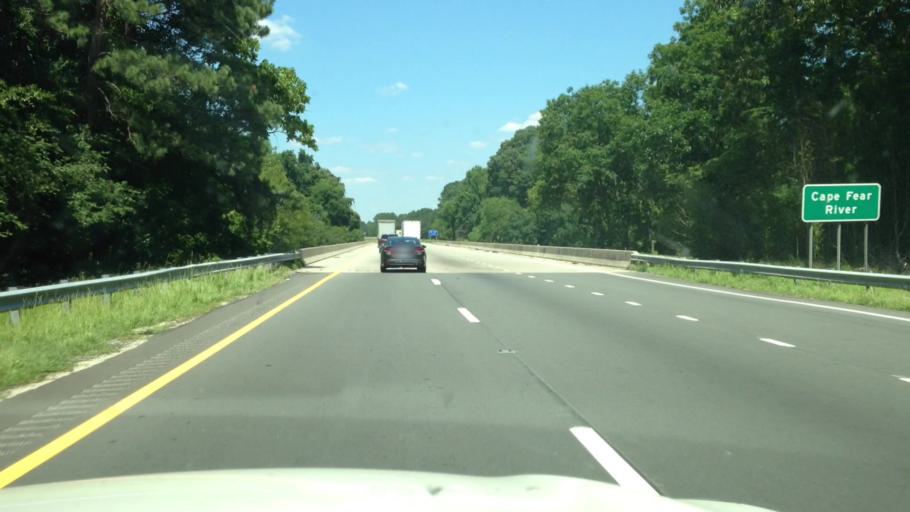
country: US
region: North Carolina
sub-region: Cumberland County
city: Vander
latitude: 34.9812
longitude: -78.8490
